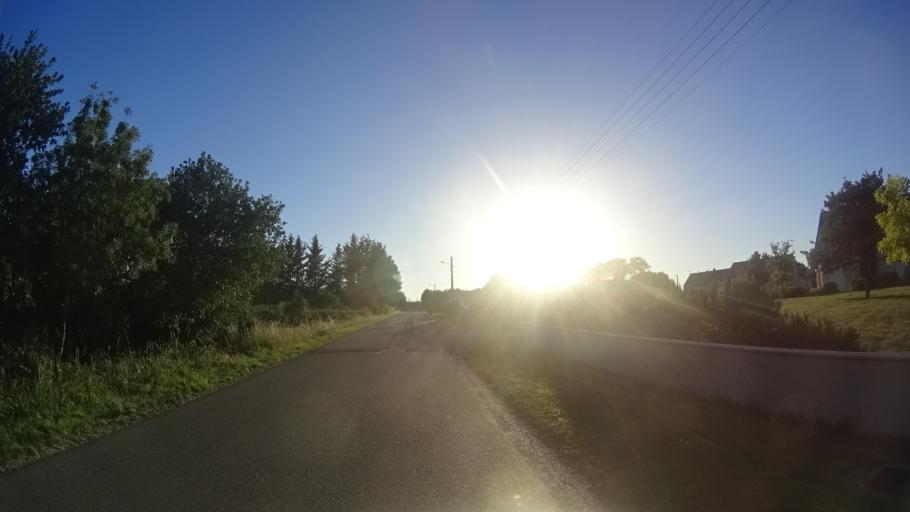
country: FR
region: Brittany
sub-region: Departement d'Ille-et-Vilaine
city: Langon
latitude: 47.7181
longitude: -1.8573
